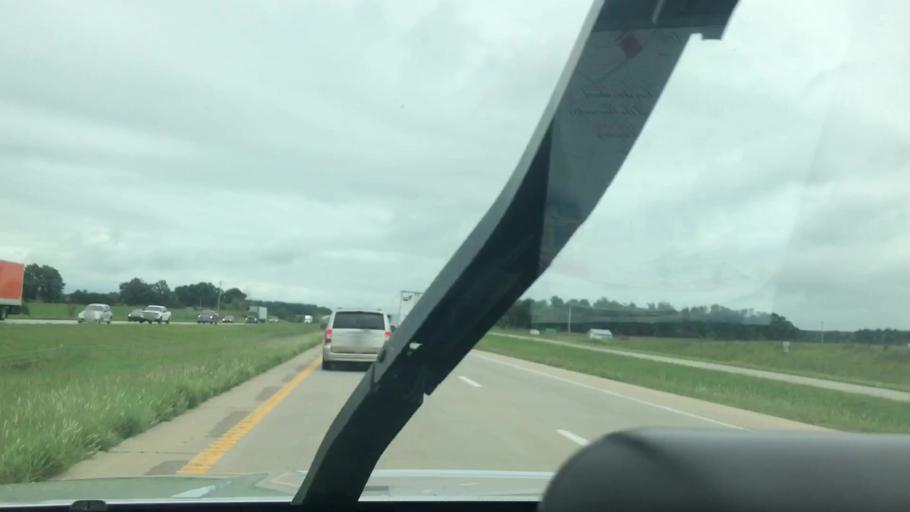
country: US
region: Missouri
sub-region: Jasper County
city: Sarcoxie
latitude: 37.0755
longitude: -93.9900
